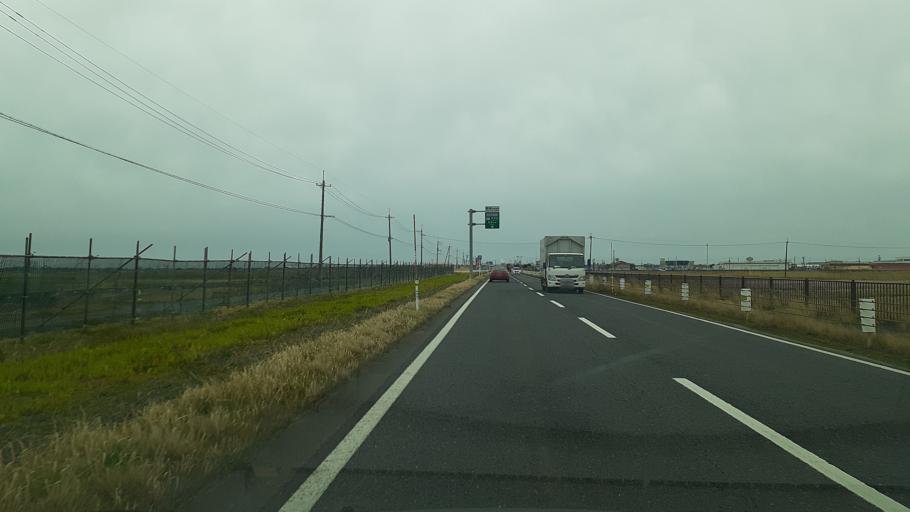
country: JP
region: Niigata
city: Niitsu-honcho
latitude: 37.8089
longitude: 139.1012
